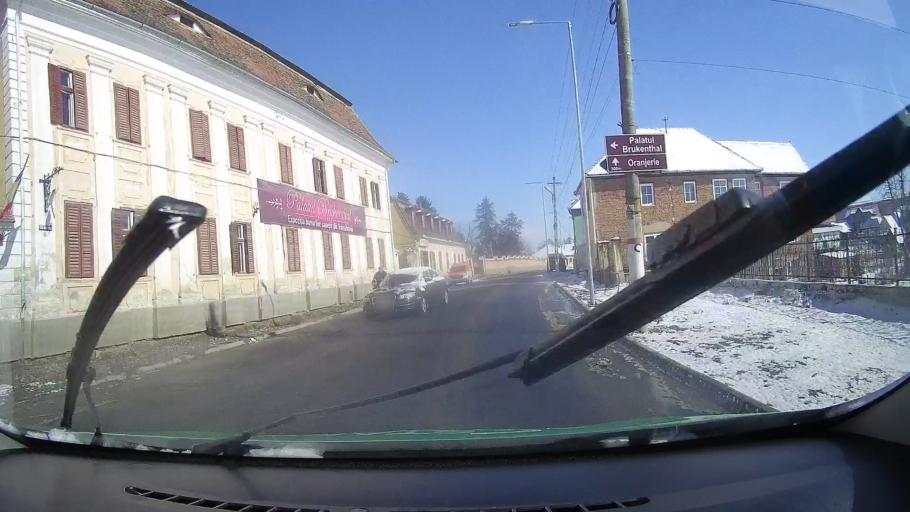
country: RO
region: Sibiu
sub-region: Comuna Avrig
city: Avrig
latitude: 45.7290
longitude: 24.3772
